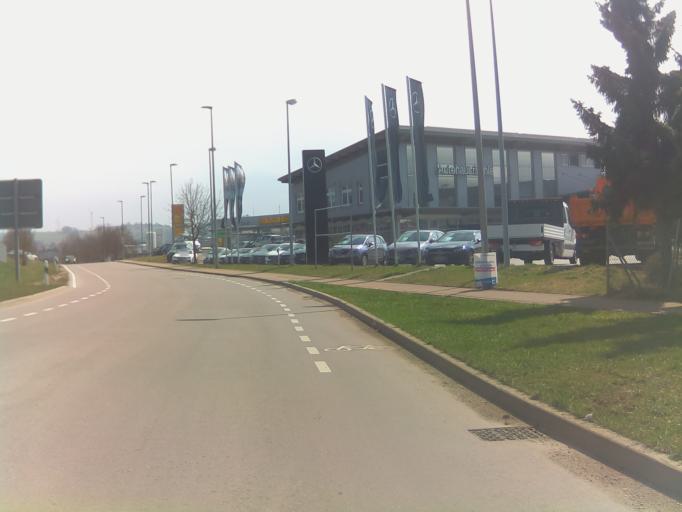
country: DE
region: Baden-Wuerttemberg
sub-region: Tuebingen Region
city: Munsingen
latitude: 48.4162
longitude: 9.4745
